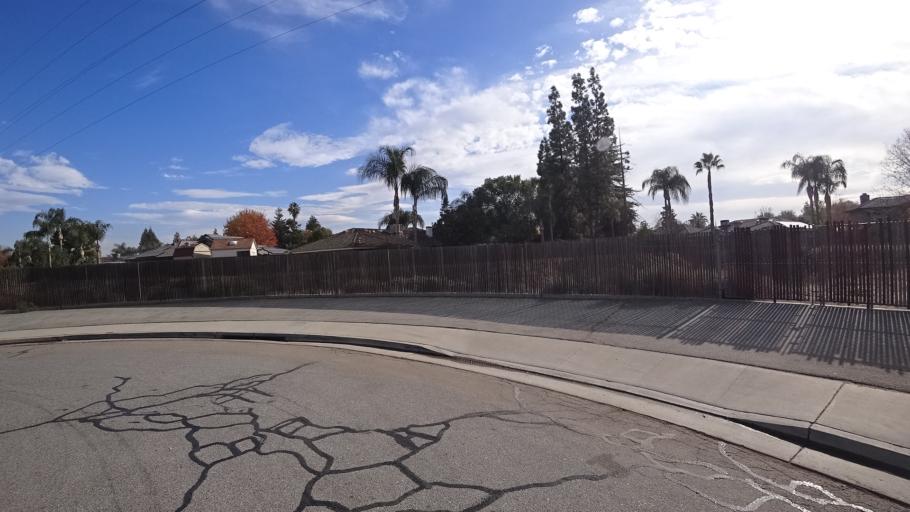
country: US
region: California
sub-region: Kern County
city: Greenacres
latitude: 35.4237
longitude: -119.0895
